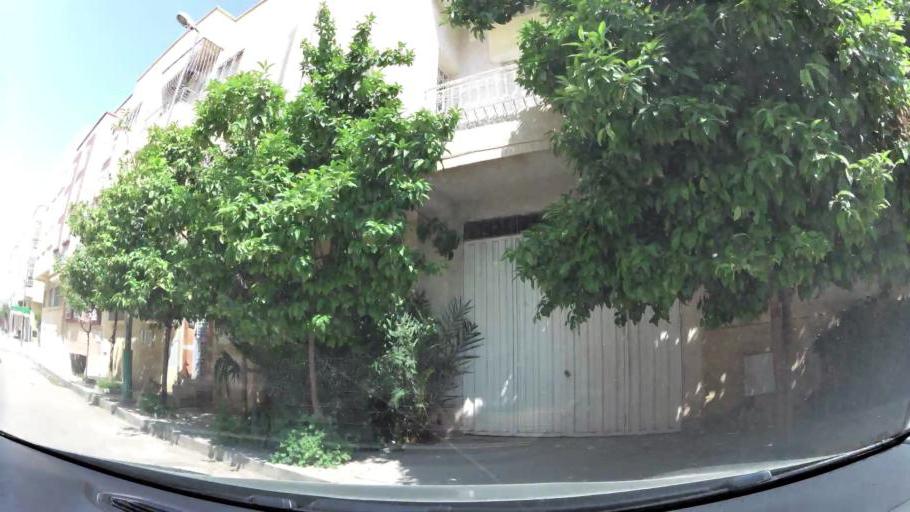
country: MA
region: Fes-Boulemane
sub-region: Fes
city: Fes
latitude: 34.0595
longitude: -5.0203
